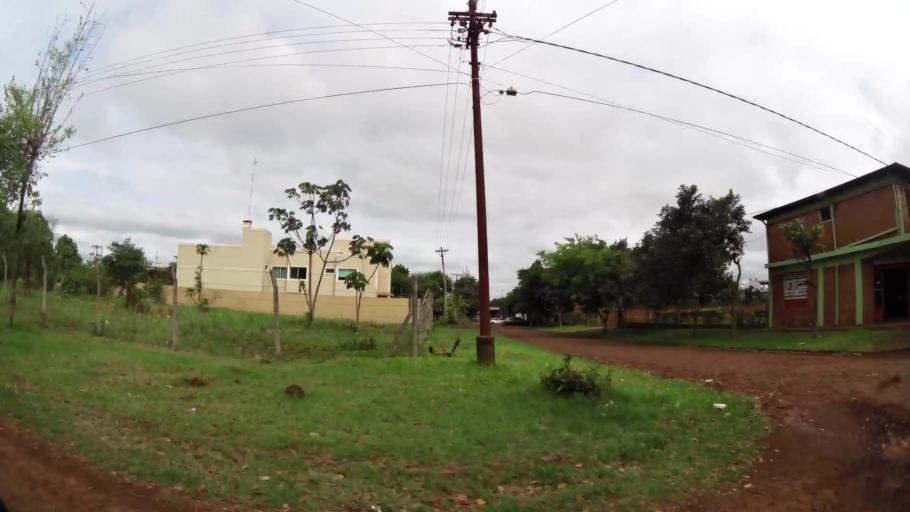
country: PY
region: Alto Parana
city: Ciudad del Este
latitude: -25.3933
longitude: -54.6379
